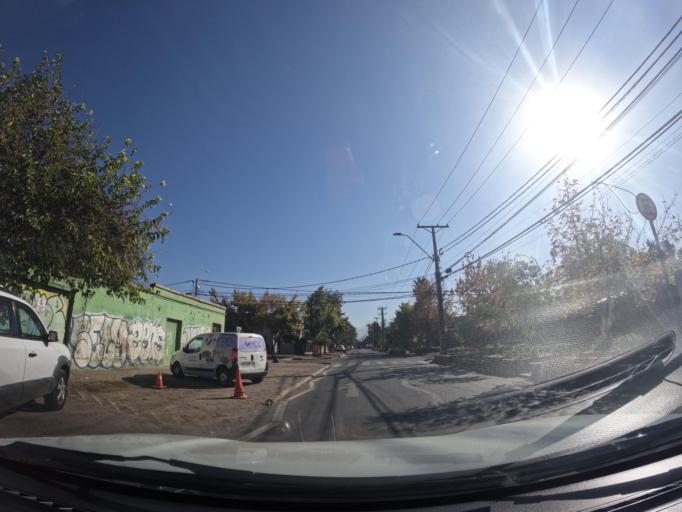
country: CL
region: Santiago Metropolitan
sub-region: Provincia de Santiago
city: Villa Presidente Frei, Nunoa, Santiago, Chile
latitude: -33.4631
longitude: -70.5680
